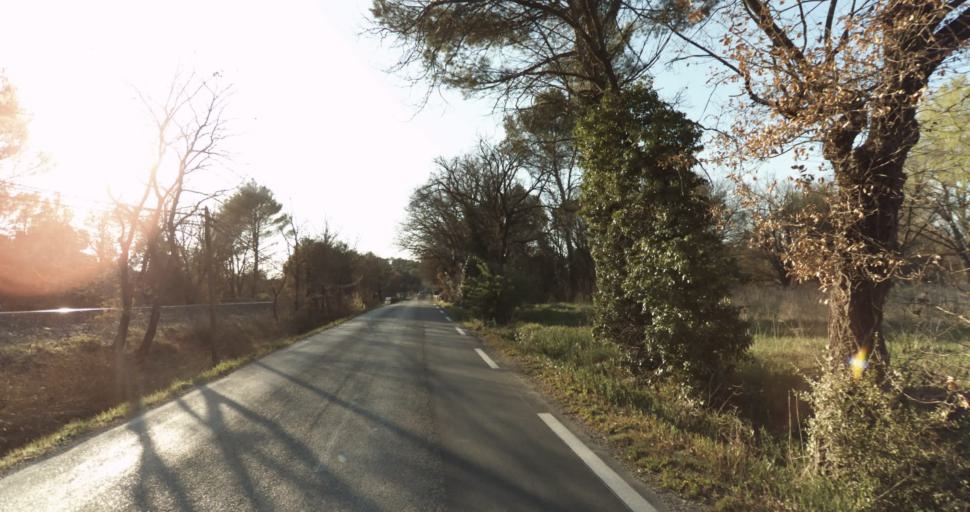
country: FR
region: Provence-Alpes-Cote d'Azur
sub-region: Departement des Bouches-du-Rhone
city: Ventabren
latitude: 43.5039
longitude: 5.3404
